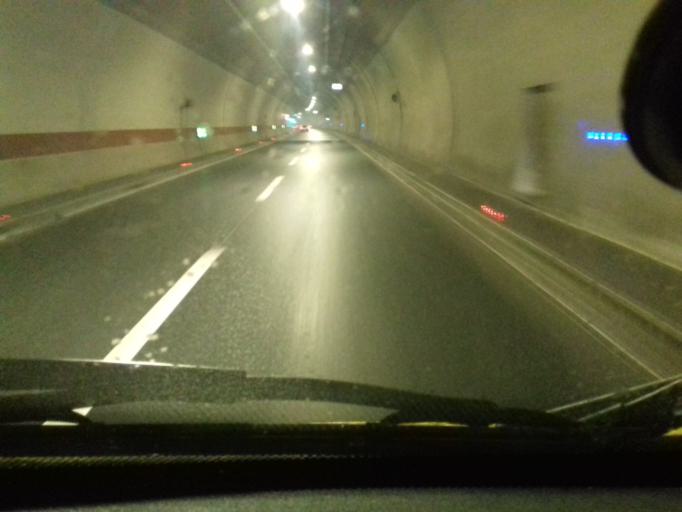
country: BA
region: Federation of Bosnia and Herzegovina
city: Zenica
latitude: 44.1514
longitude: 17.9659
